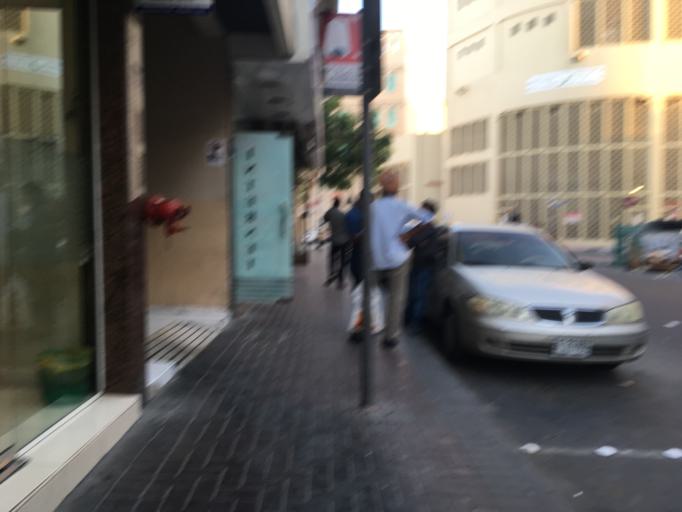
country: AE
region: Ash Shariqah
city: Sharjah
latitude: 25.2619
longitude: 55.2987
